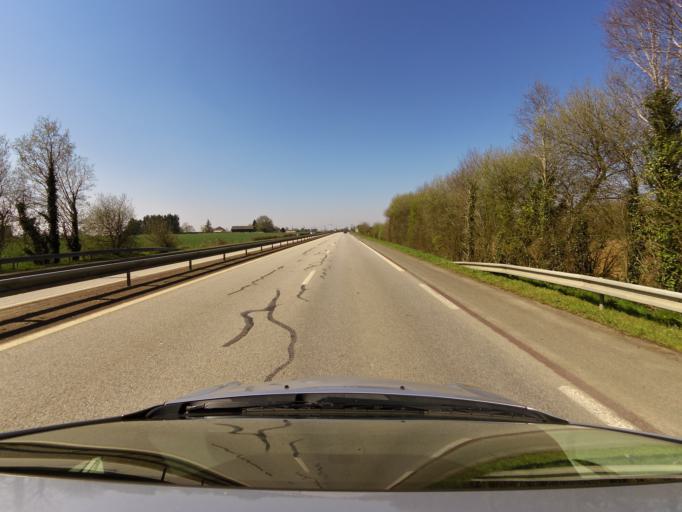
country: FR
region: Brittany
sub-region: Departement du Morbihan
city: Pleugriffet
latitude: 47.9230
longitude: -2.6634
